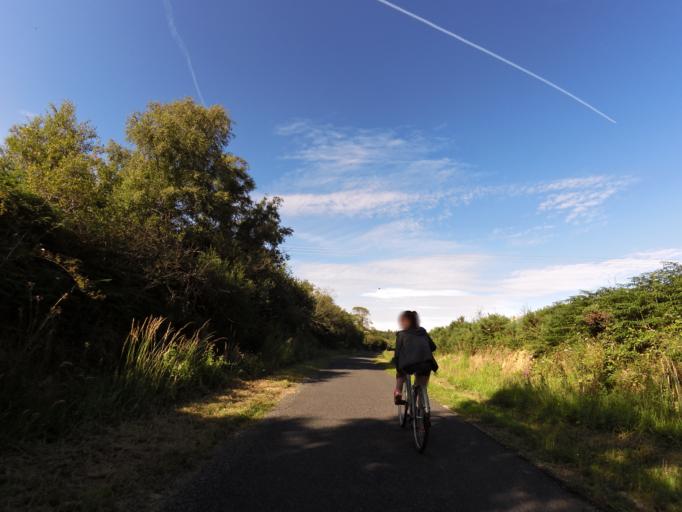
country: IE
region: Munster
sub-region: Waterford
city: Portlaw
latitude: 52.2364
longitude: -7.3008
